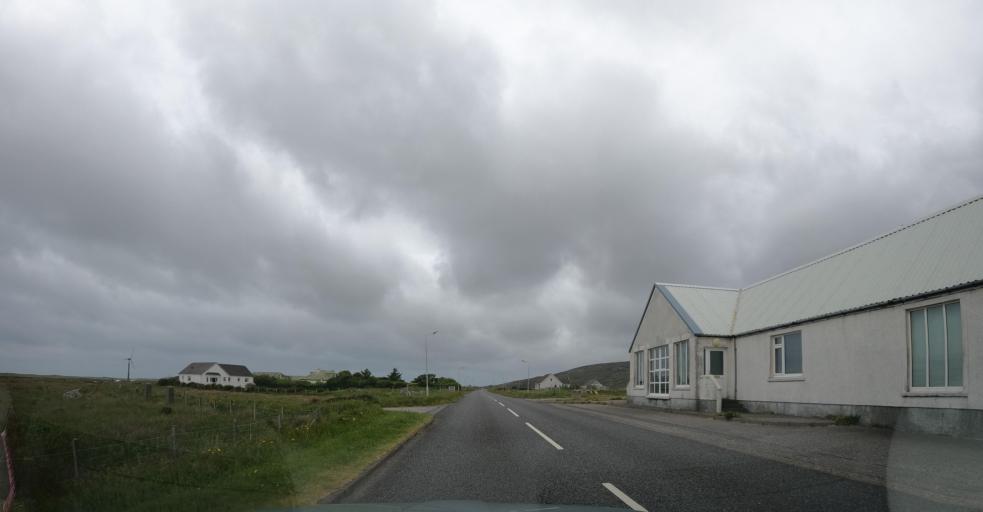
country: GB
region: Scotland
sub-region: Eilean Siar
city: Isle of South Uist
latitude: 57.1736
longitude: -7.3756
